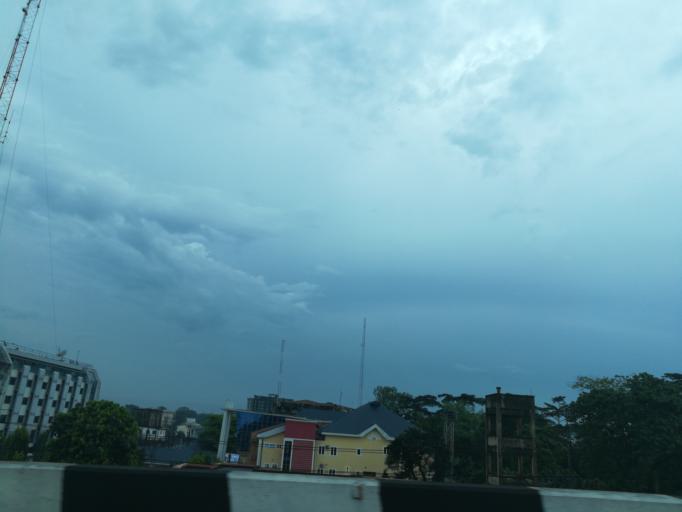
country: NG
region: Rivers
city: Port Harcourt
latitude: 4.7885
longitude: 7.0034
